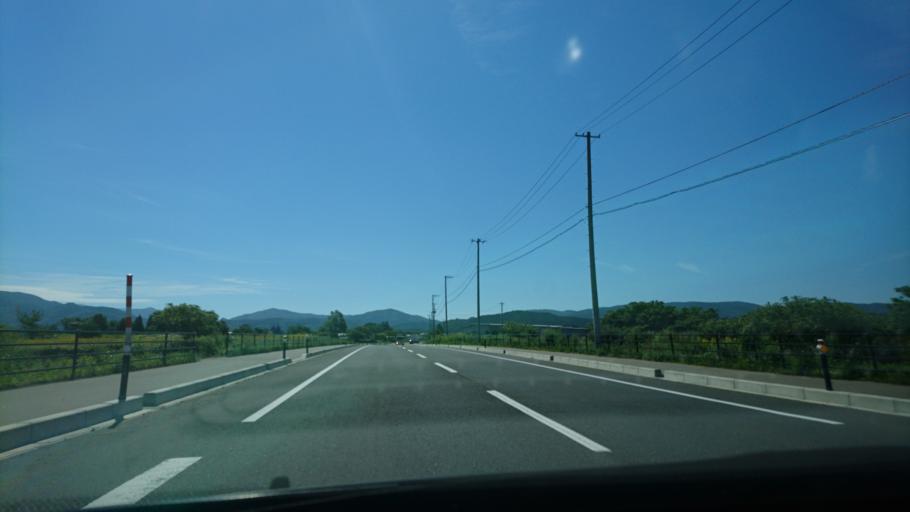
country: JP
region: Iwate
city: Tono
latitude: 39.2999
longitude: 141.5777
